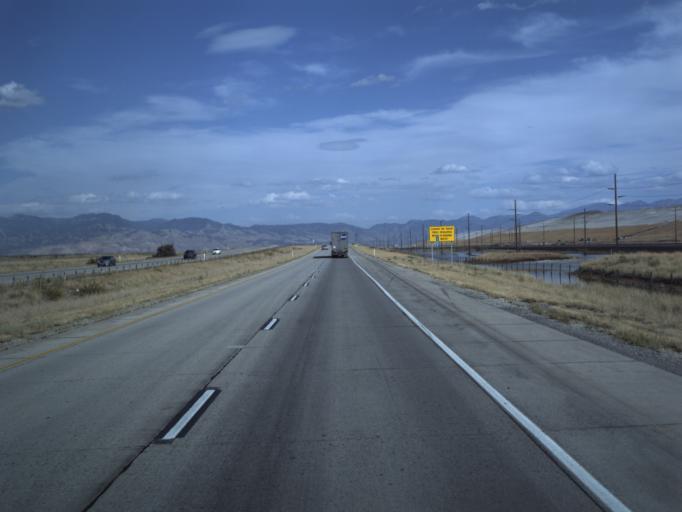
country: US
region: Utah
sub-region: Salt Lake County
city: Magna
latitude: 40.7706
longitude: -112.1461
